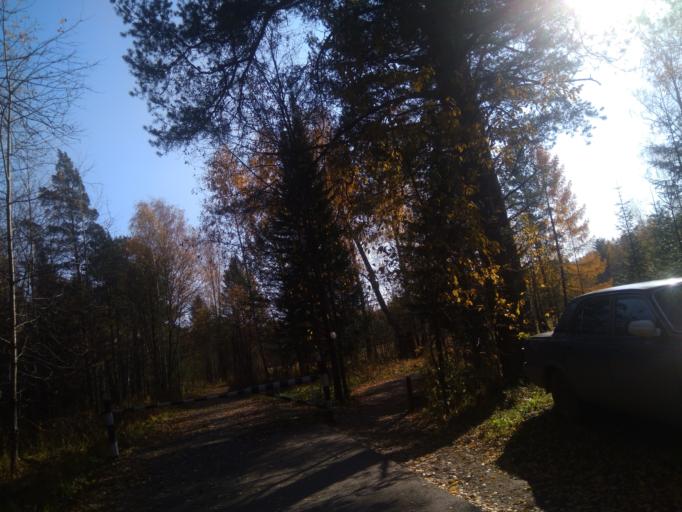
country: RU
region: Sverdlovsk
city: Mikhaylovsk
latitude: 56.5227
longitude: 59.2347
